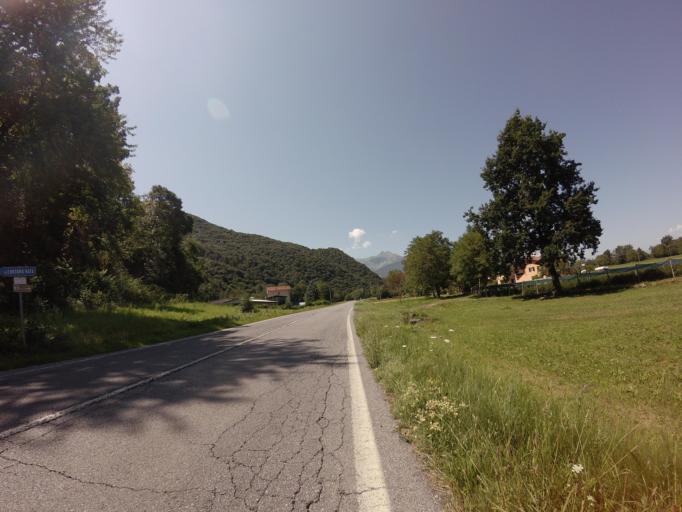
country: IT
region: Piedmont
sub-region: Provincia di Cuneo
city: Chiusa di Pesio
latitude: 44.3326
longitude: 7.6889
